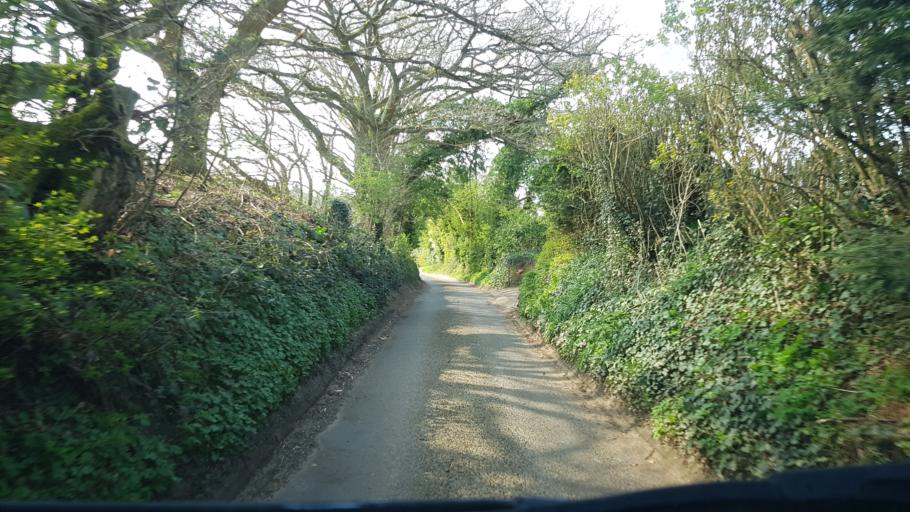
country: GB
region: England
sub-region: Surrey
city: Chilworth
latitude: 51.2248
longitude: -0.5131
